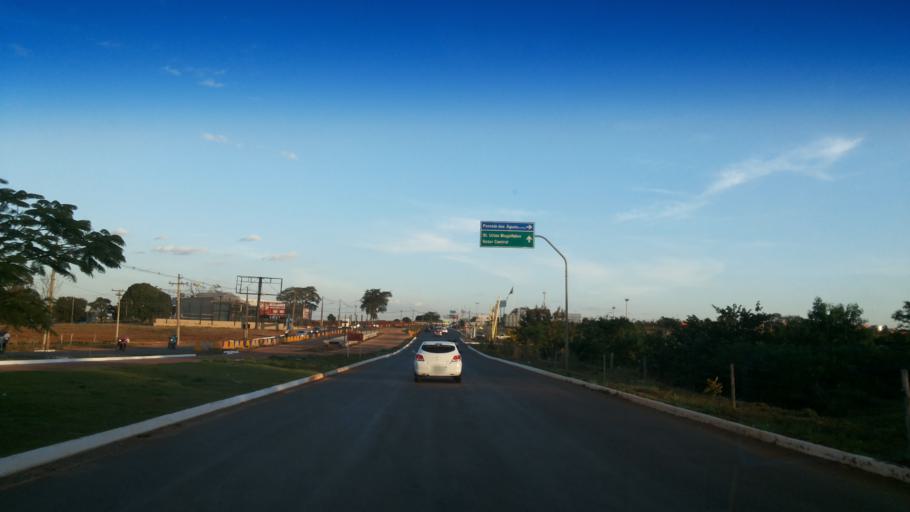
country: BR
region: Goias
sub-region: Goiania
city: Goiania
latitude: -16.6255
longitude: -49.2743
